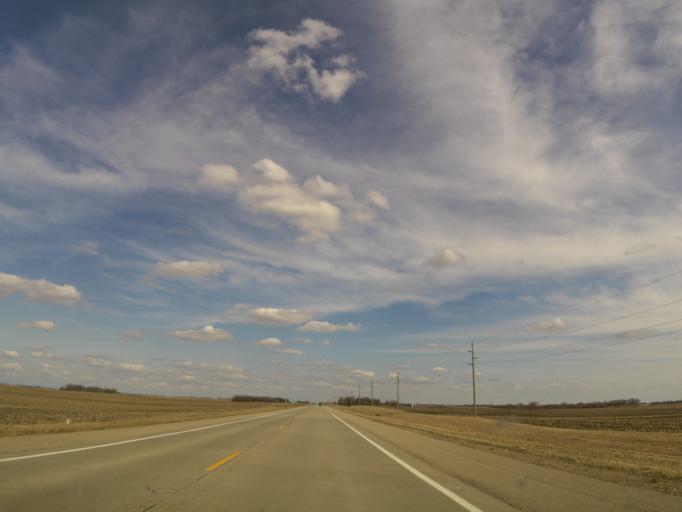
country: US
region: Minnesota
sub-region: Lac qui Parle County
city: Dawson
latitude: 44.9357
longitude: -96.1217
